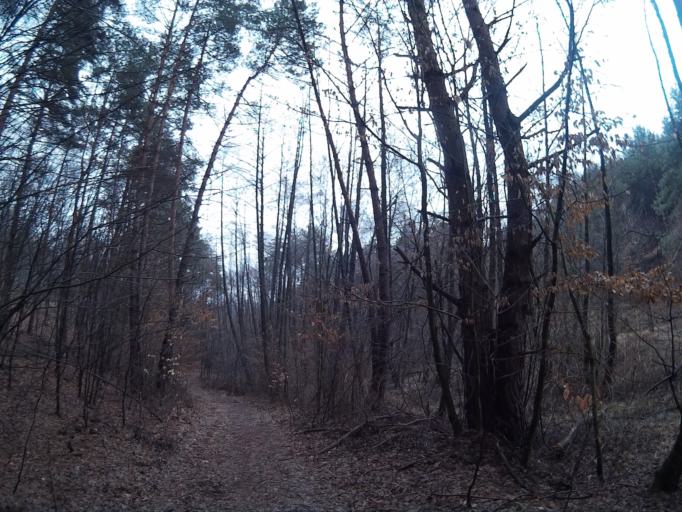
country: HU
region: Borsod-Abauj-Zemplen
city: Sarospatak
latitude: 48.4666
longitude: 21.4709
